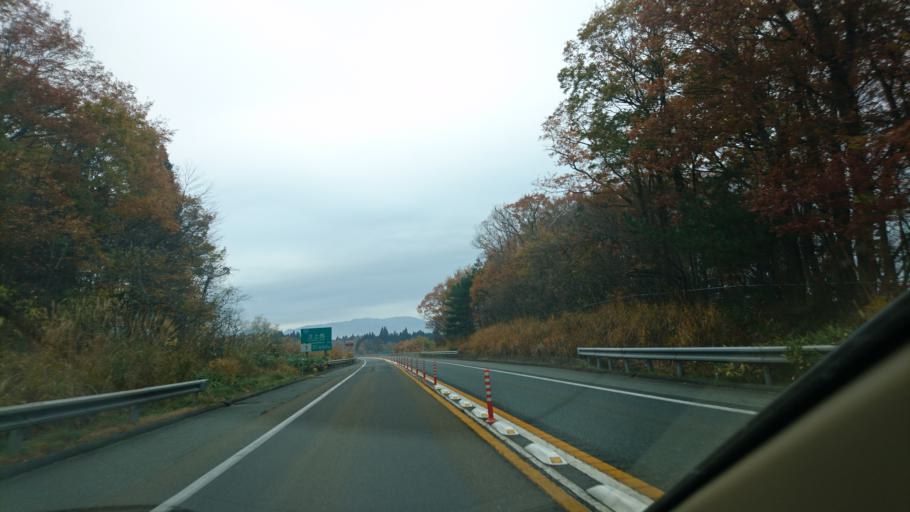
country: JP
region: Iwate
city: Kitakami
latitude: 39.2875
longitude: 140.9928
